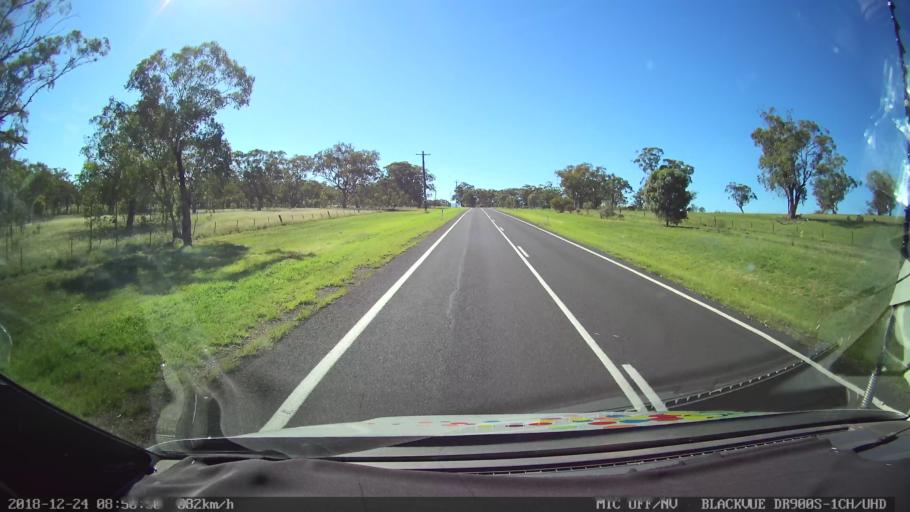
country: AU
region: New South Wales
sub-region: Liverpool Plains
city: Quirindi
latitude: -31.4792
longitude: 150.6689
